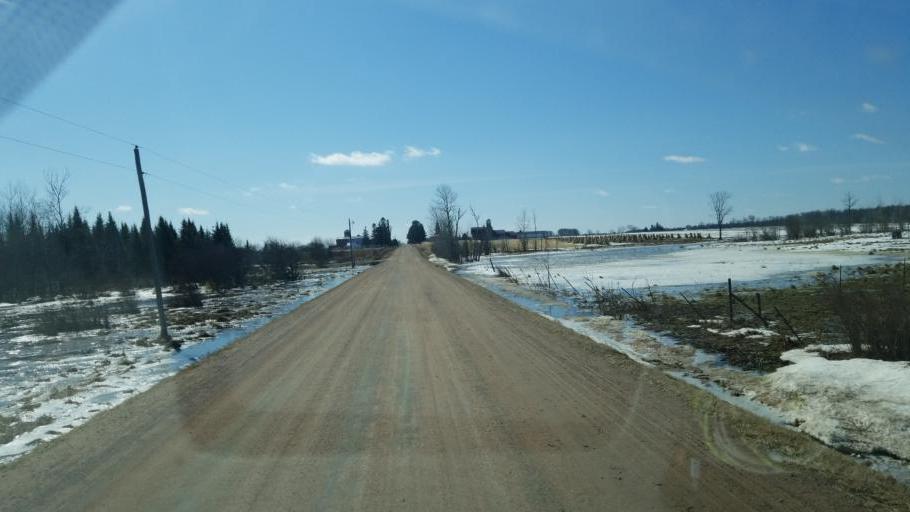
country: US
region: Wisconsin
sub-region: Clark County
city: Loyal
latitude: 44.6531
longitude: -90.3978
